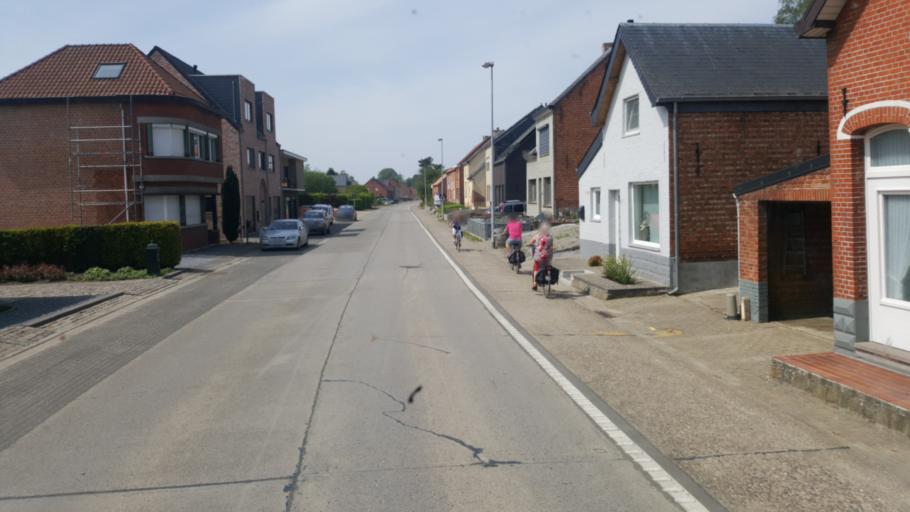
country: BE
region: Flanders
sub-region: Provincie Antwerpen
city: Hulshout
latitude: 51.0704
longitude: 4.8231
